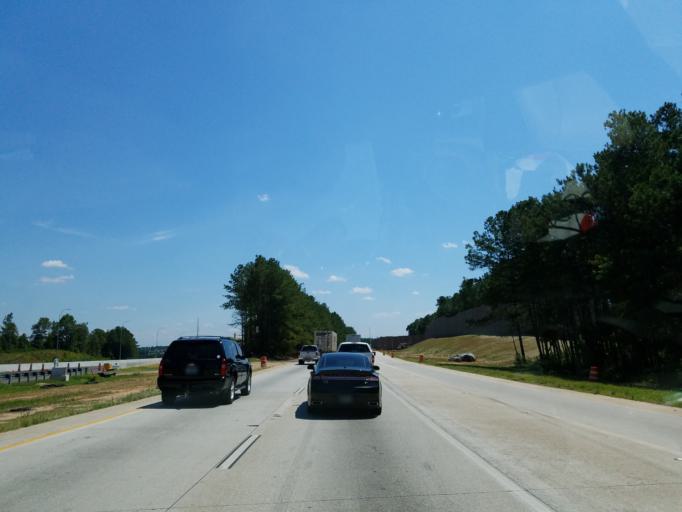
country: US
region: Georgia
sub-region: Henry County
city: Stockbridge
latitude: 33.5492
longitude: -84.2691
